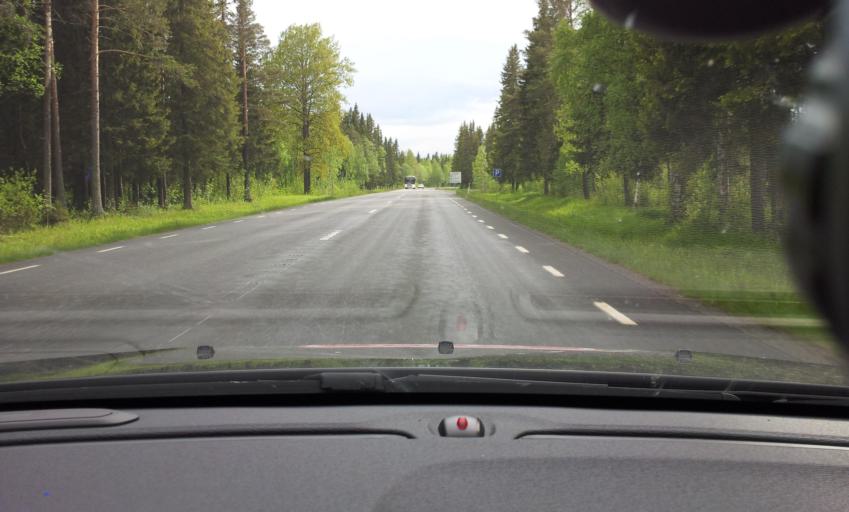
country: SE
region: Jaemtland
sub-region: OEstersunds Kommun
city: Ostersund
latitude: 63.1857
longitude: 14.7321
